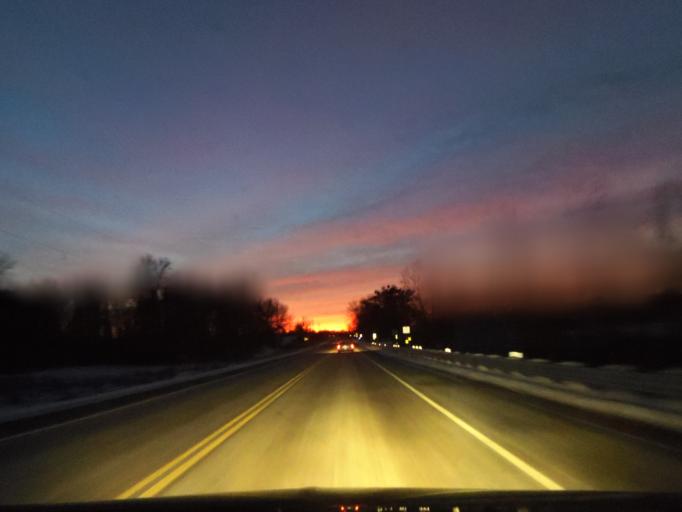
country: US
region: Minnesota
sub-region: Chisago County
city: Chisago City
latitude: 45.3422
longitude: -92.8641
